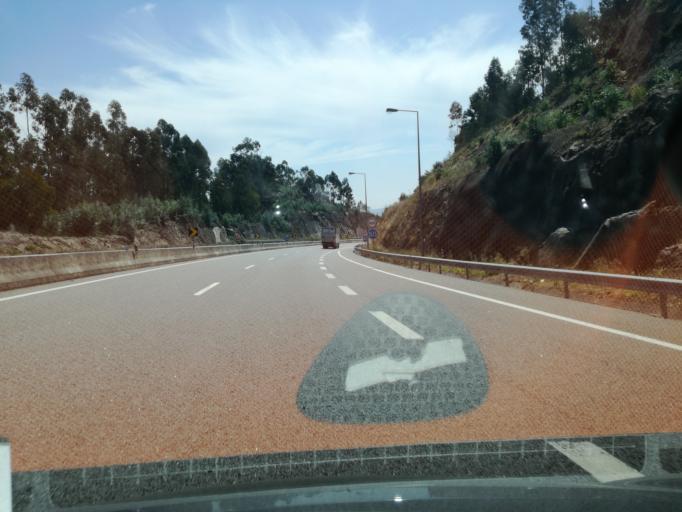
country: PT
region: Viana do Castelo
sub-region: Viana do Castelo
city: Meadela
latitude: 41.7414
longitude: -8.7934
